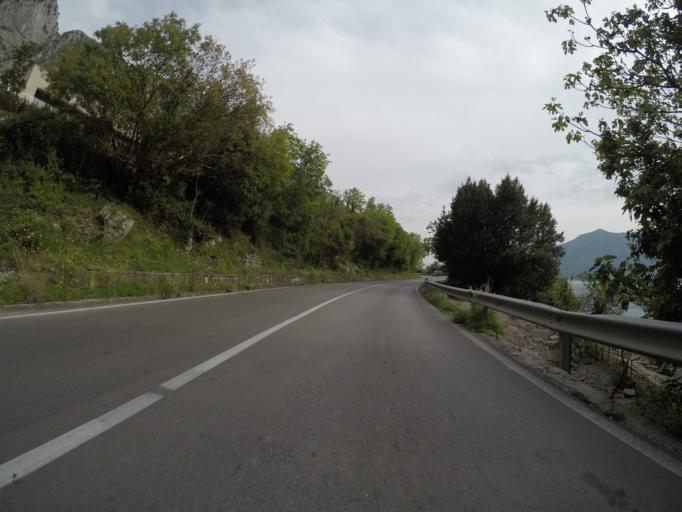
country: ME
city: Dobrota
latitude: 42.4881
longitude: 18.7652
